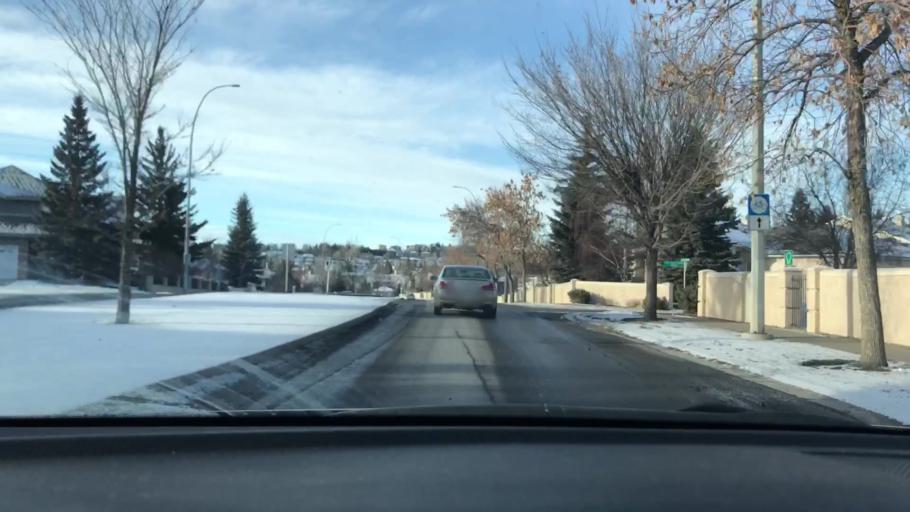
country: CA
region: Alberta
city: Calgary
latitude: 51.0196
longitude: -114.1775
